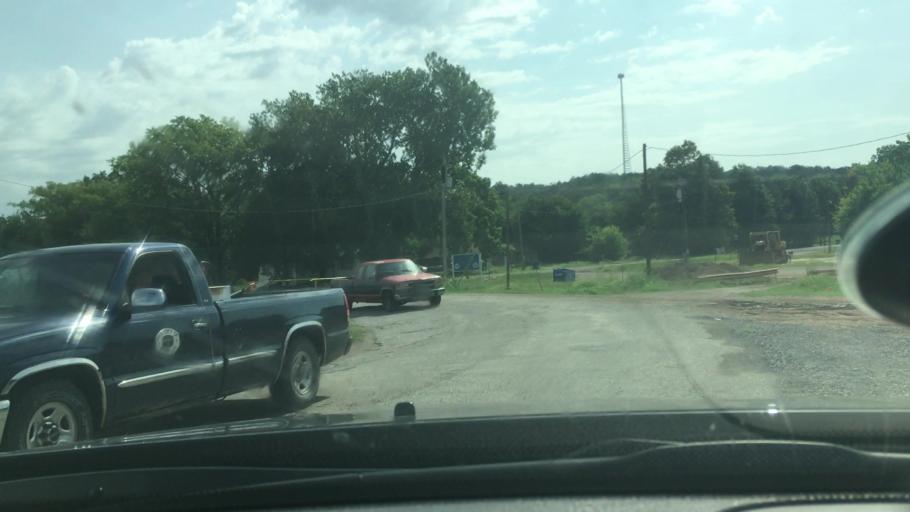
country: US
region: Oklahoma
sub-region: Atoka County
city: Atoka
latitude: 34.4666
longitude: -96.0562
